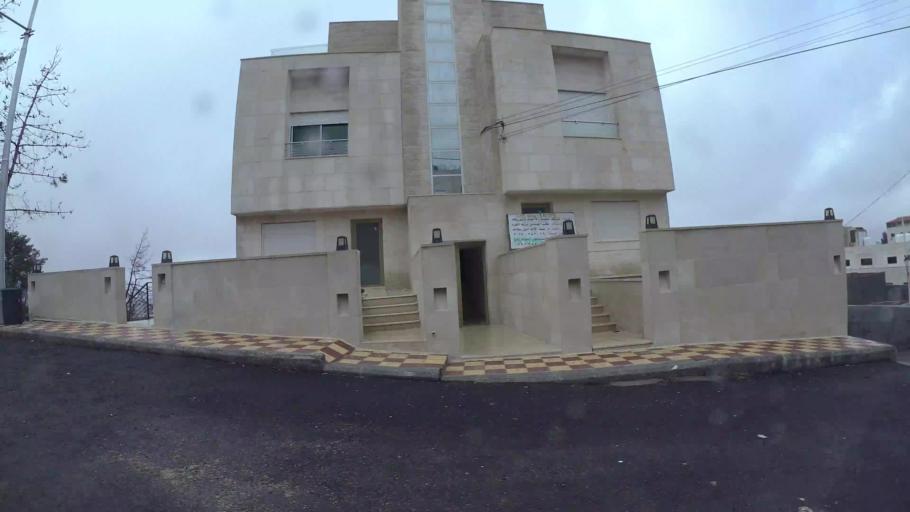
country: JO
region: Amman
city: Al Jubayhah
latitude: 32.0275
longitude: 35.8282
